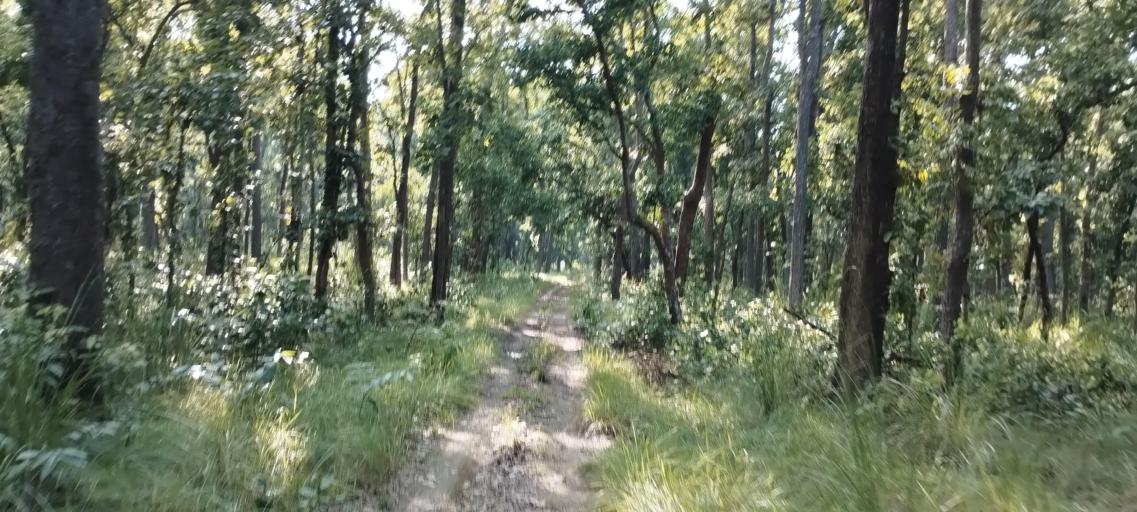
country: NP
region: Far Western
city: Tikapur
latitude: 28.5224
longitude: 81.2682
